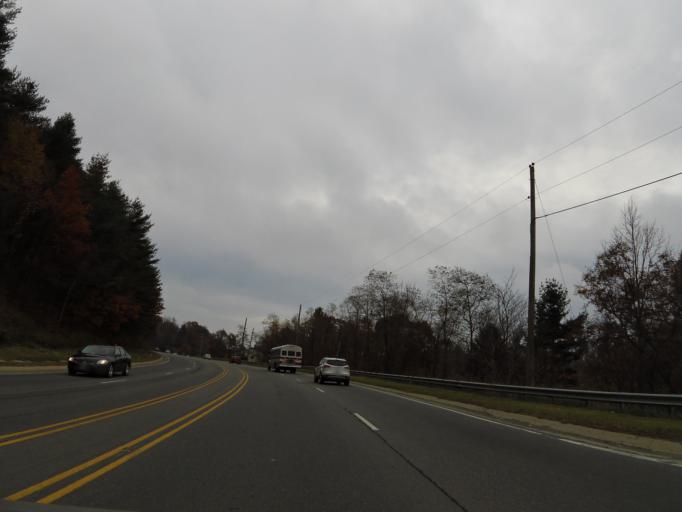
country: US
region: North Carolina
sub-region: Watauga County
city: Boone
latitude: 36.1867
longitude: -81.6527
